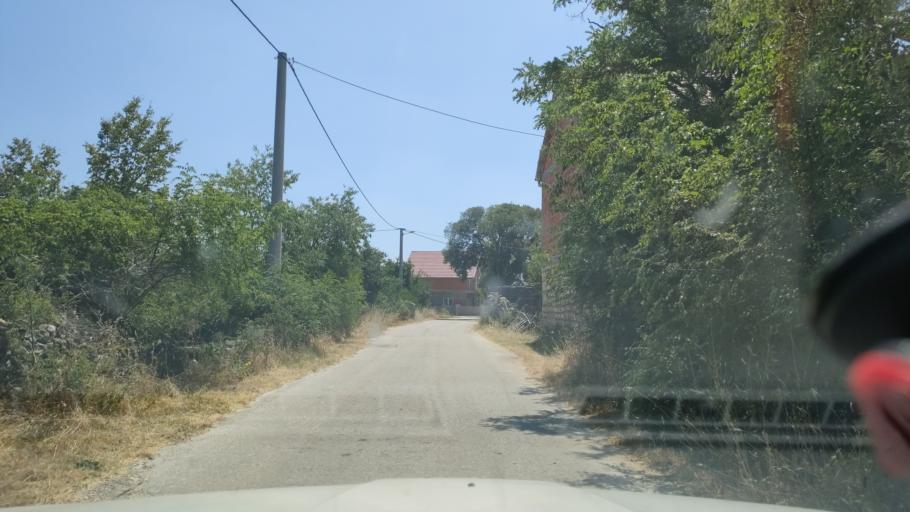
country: HR
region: Sibensko-Kniniska
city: Kistanje
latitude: 43.9529
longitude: 15.8813
